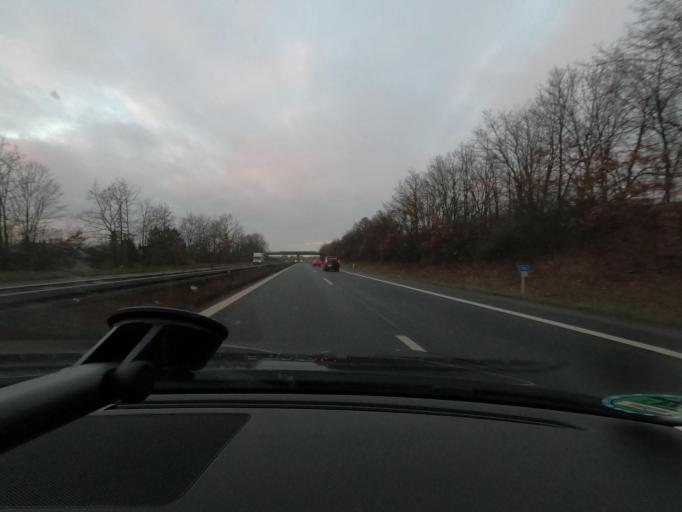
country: DE
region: Bavaria
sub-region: Upper Franconia
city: Eggolsheim
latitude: 49.7639
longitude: 11.0525
